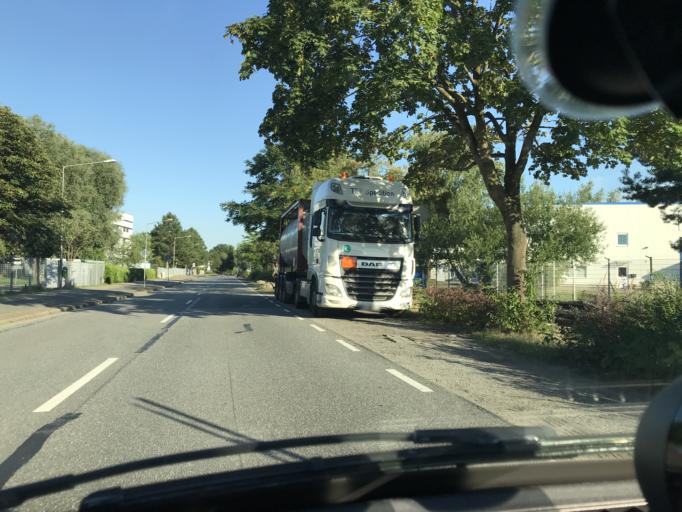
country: DE
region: Lower Saxony
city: Buxtehude
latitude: 53.4615
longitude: 9.7187
